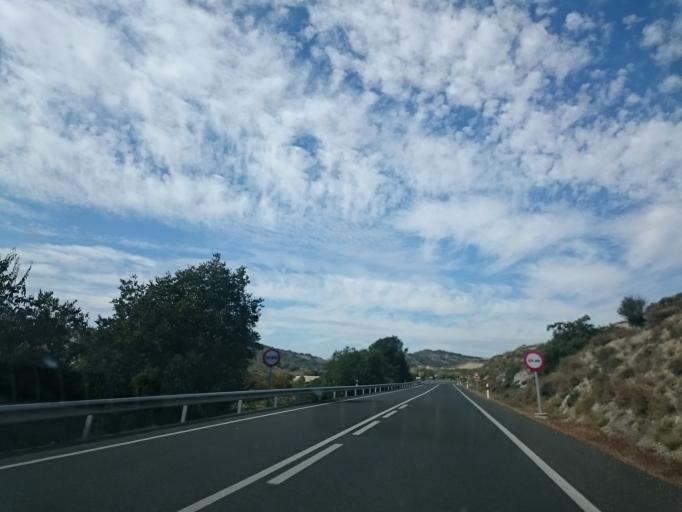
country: ES
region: Aragon
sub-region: Provincia de Huesca
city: Albelda
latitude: 41.8762
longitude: 0.5204
